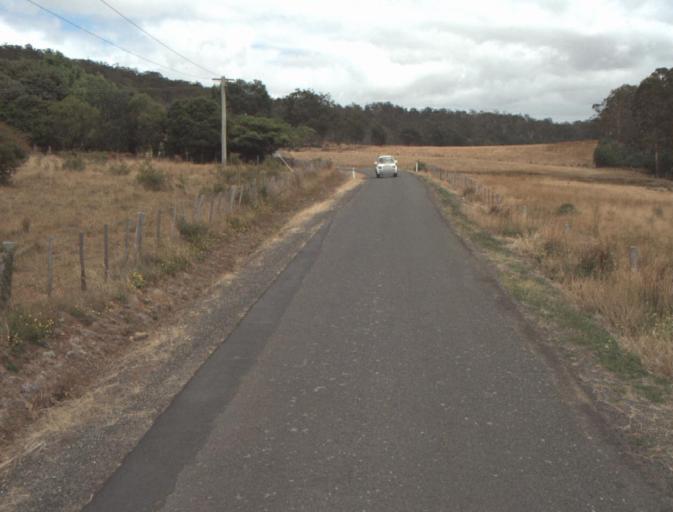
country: AU
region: Tasmania
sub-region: Northern Midlands
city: Evandale
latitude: -41.5214
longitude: 147.3930
